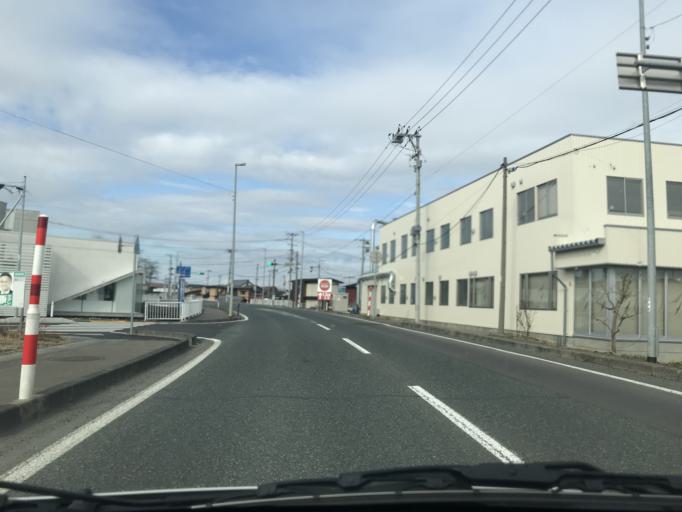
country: JP
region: Iwate
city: Hanamaki
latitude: 39.3848
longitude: 141.1249
